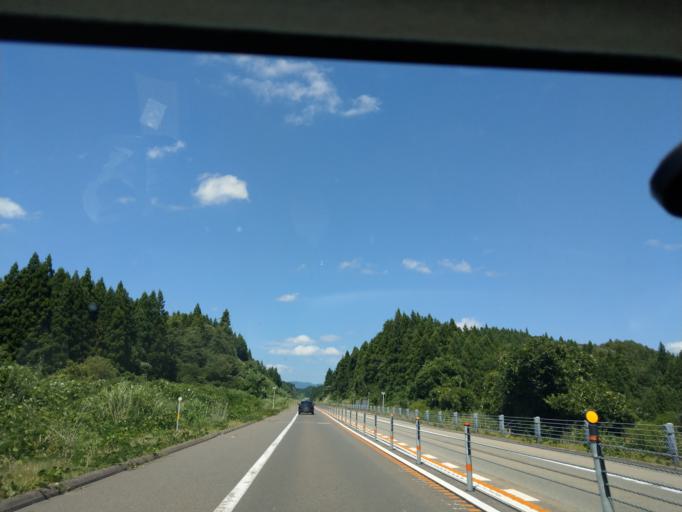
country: JP
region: Akita
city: Akita
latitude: 39.6868
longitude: 140.1857
